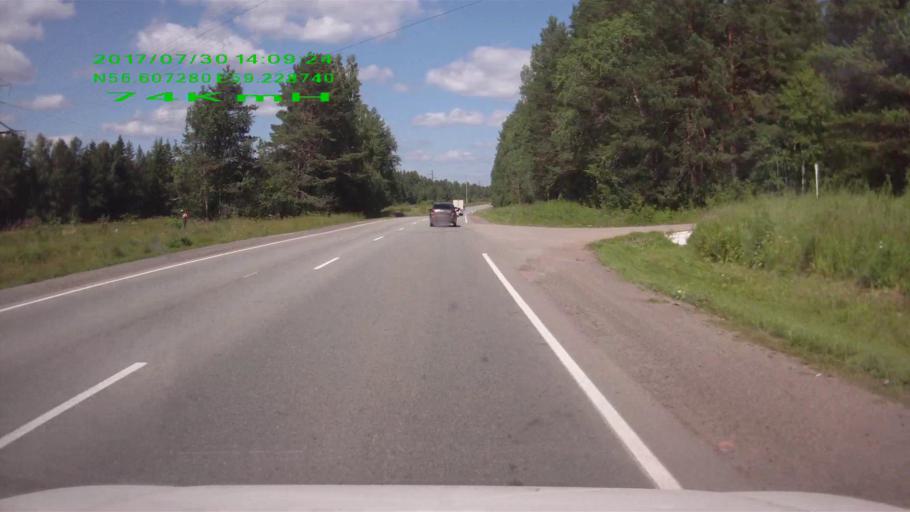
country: RU
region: Sverdlovsk
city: Nizhniye Sergi
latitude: 56.6077
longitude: 59.2287
